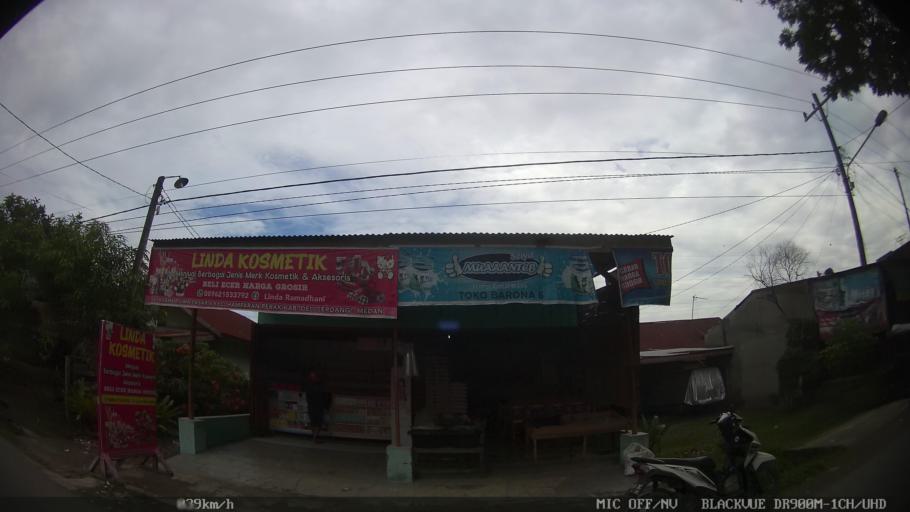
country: ID
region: North Sumatra
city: Sunggal
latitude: 3.6189
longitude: 98.6031
